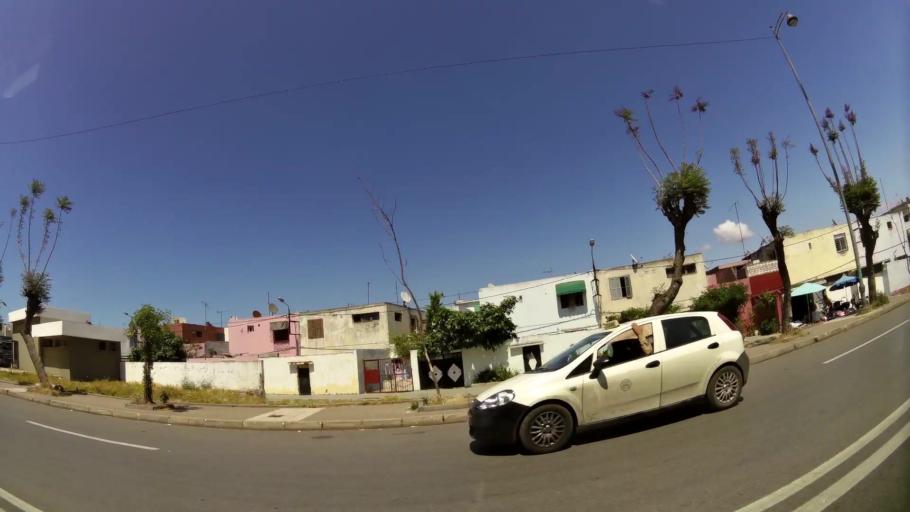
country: MA
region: Gharb-Chrarda-Beni Hssen
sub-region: Kenitra Province
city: Kenitra
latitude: 34.2482
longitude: -6.5545
